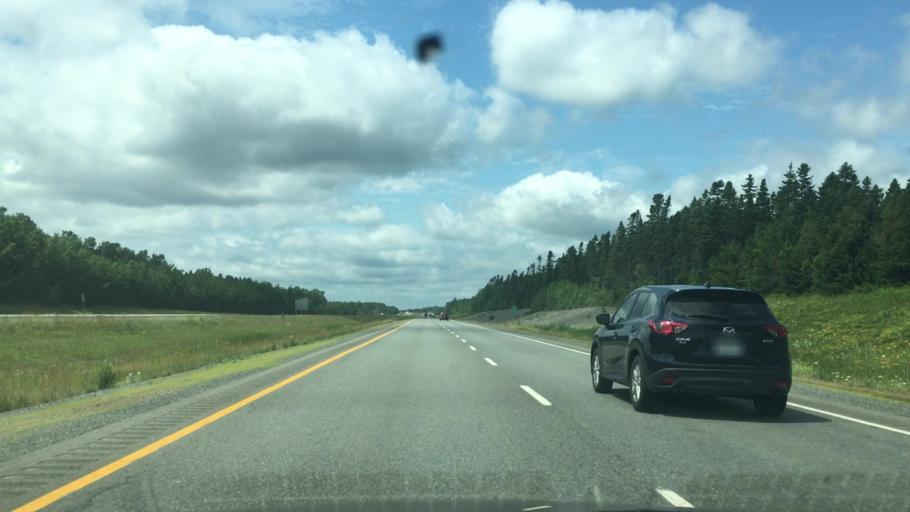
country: CA
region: Nova Scotia
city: Oxford
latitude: 45.7159
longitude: -63.9244
